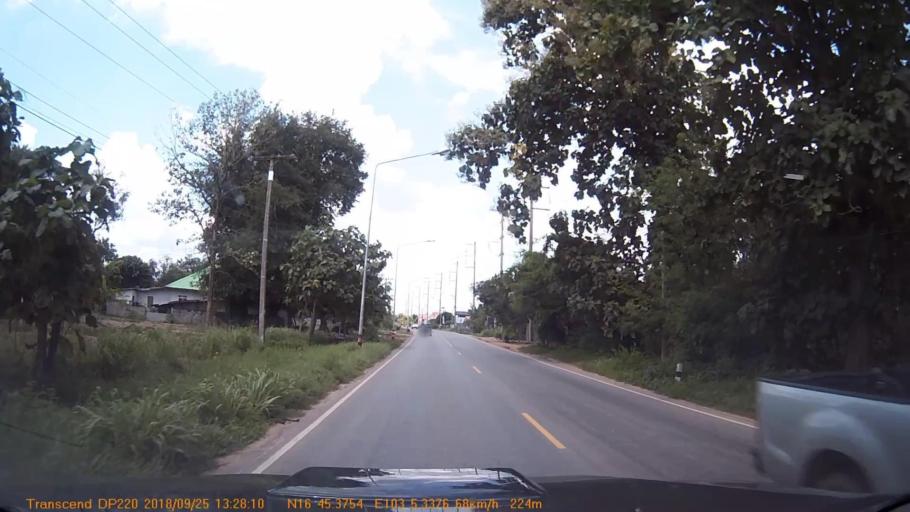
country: TH
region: Khon Kaen
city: Kranuan
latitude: 16.7561
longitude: 103.0890
